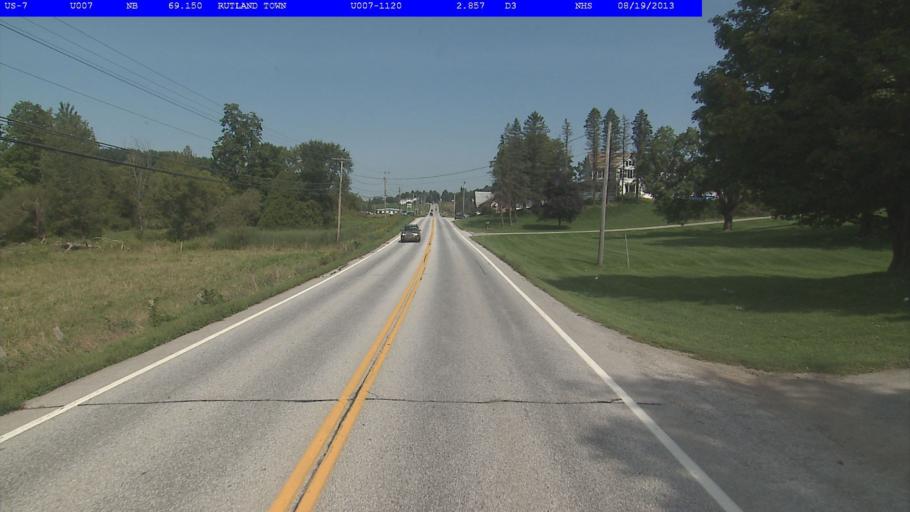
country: US
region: Vermont
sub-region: Rutland County
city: Rutland
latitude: 43.6518
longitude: -72.9859
